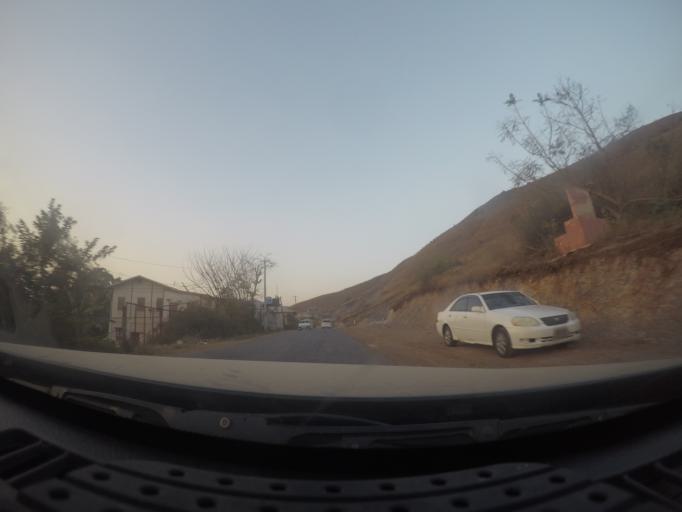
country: MM
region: Shan
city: Taunggyi
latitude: 20.7279
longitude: 97.0564
